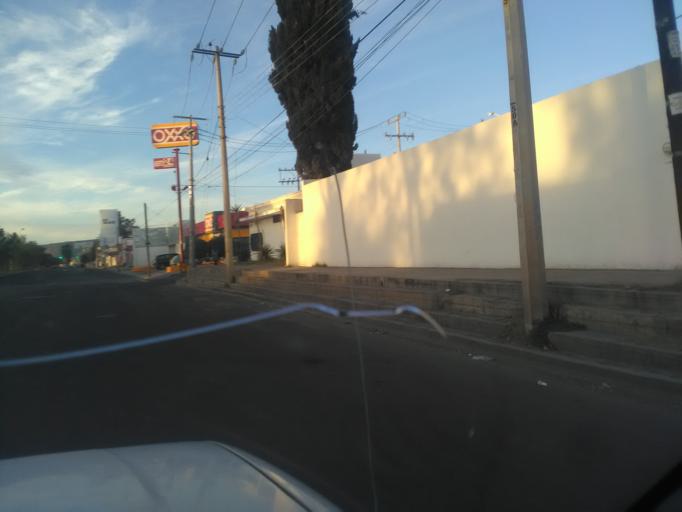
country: MX
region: Durango
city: Victoria de Durango
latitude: 23.9922
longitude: -104.6636
